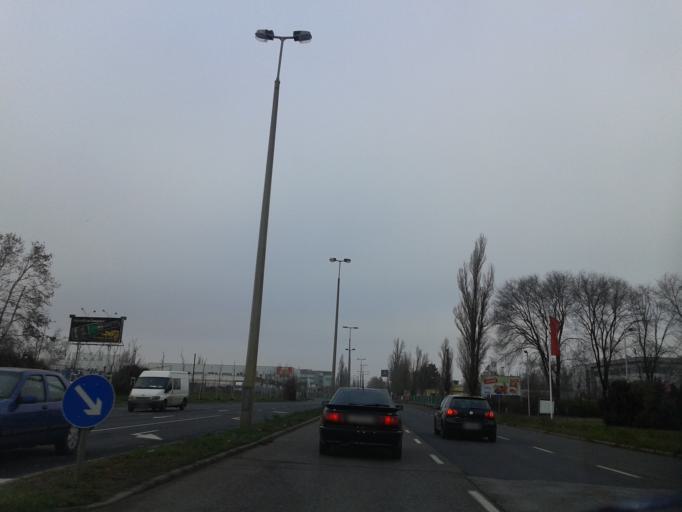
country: HU
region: Budapest
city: Budapest XXII. keruelet
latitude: 47.4410
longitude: 19.0454
